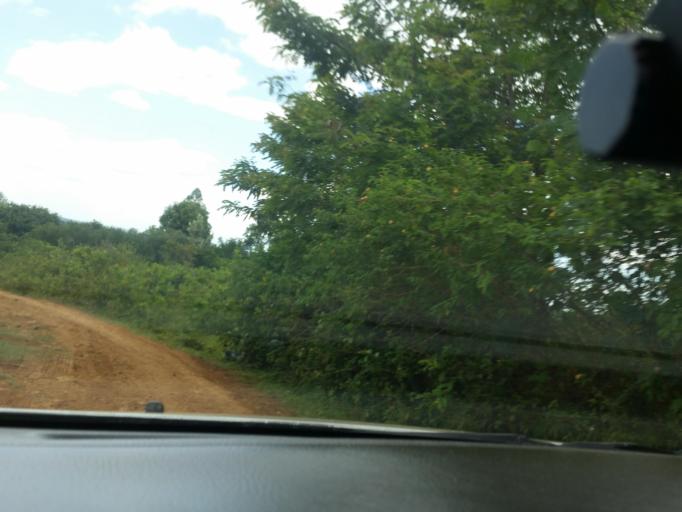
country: KE
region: Siaya
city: Yala
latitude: 0.1051
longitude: 34.4117
